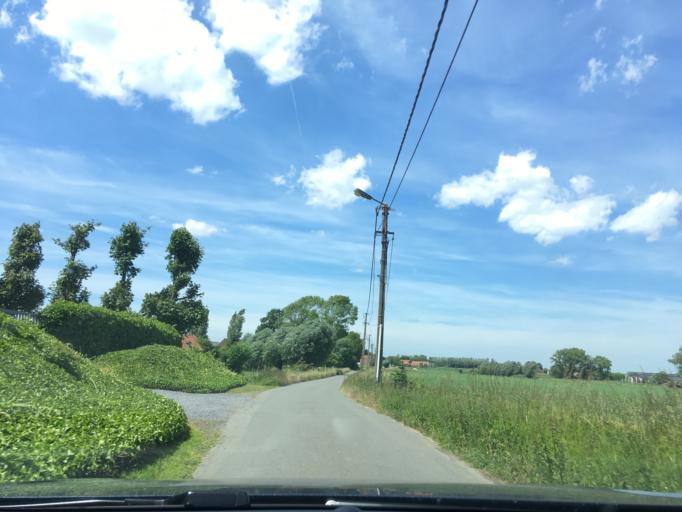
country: BE
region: Flanders
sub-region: Provincie West-Vlaanderen
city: Lichtervelde
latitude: 51.0238
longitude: 3.1768
